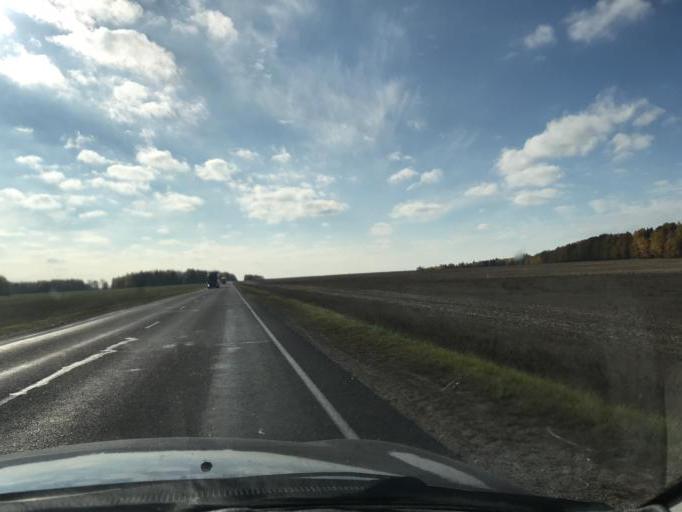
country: BY
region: Grodnenskaya
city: Voranava
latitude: 54.1976
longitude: 25.3467
